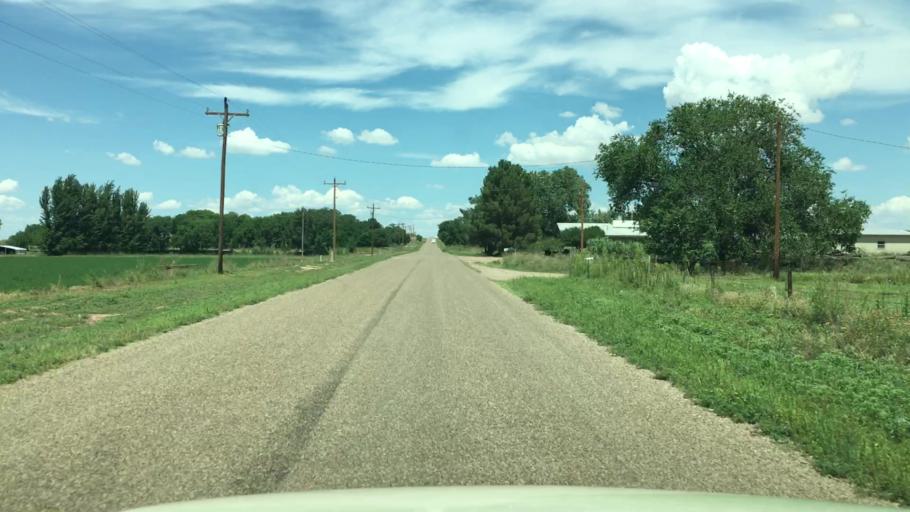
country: US
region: New Mexico
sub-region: De Baca County
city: Fort Sumner
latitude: 34.4443
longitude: -104.1936
